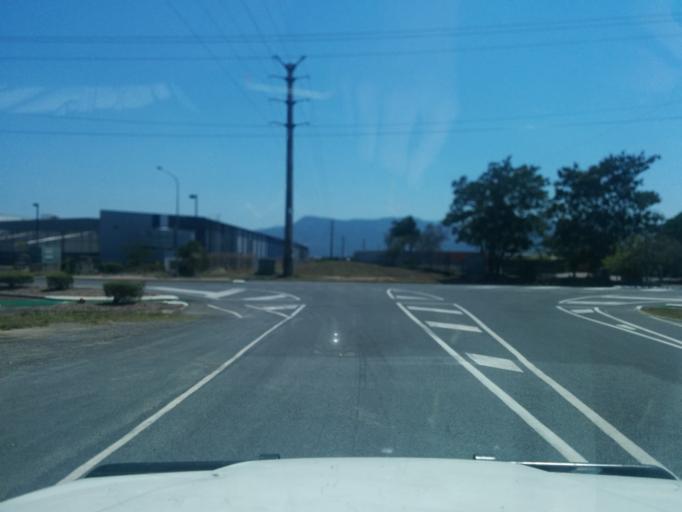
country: AU
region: Queensland
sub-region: Cairns
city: Cairns
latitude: -16.9307
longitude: 145.7726
